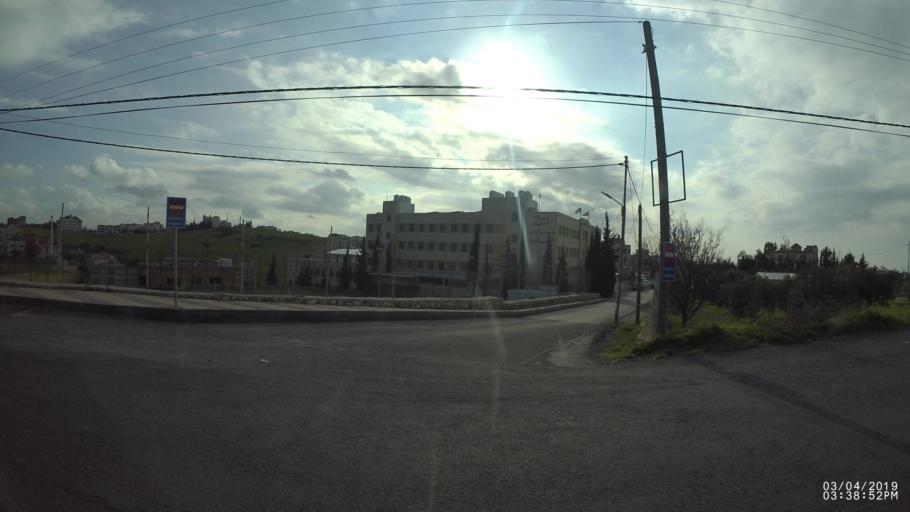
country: JO
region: Amman
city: Umm as Summaq
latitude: 31.9171
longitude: 35.8491
